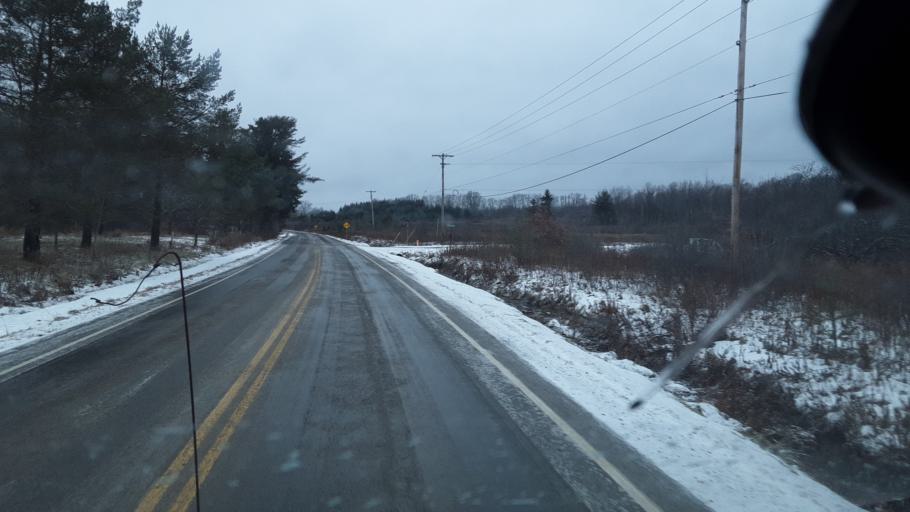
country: US
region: New York
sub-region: Allegany County
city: Friendship
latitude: 42.2325
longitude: -78.1424
